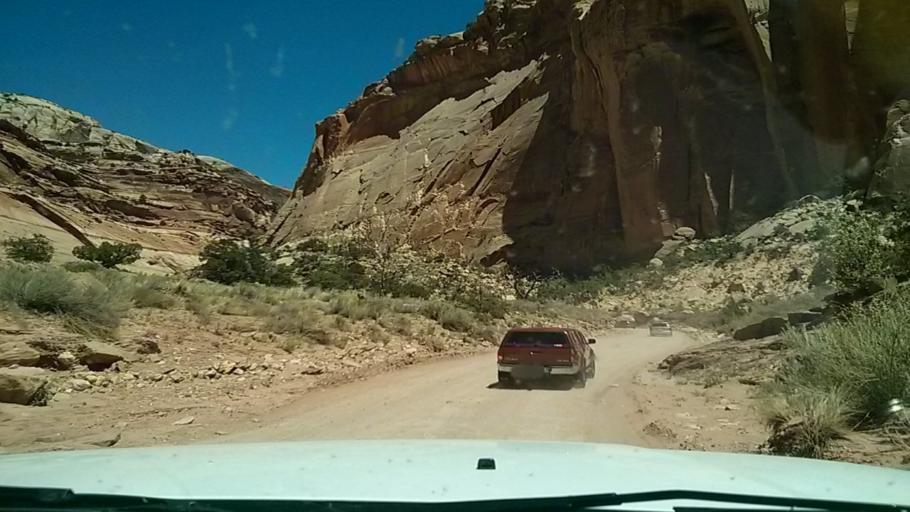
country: US
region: Utah
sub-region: Wayne County
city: Loa
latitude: 38.2099
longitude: -111.1917
